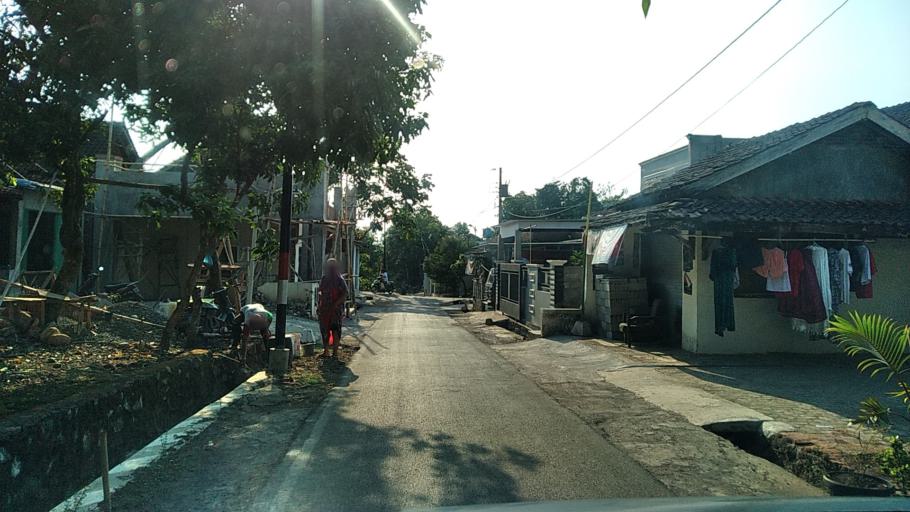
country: ID
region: Central Java
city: Ungaran
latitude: -7.0713
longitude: 110.3545
